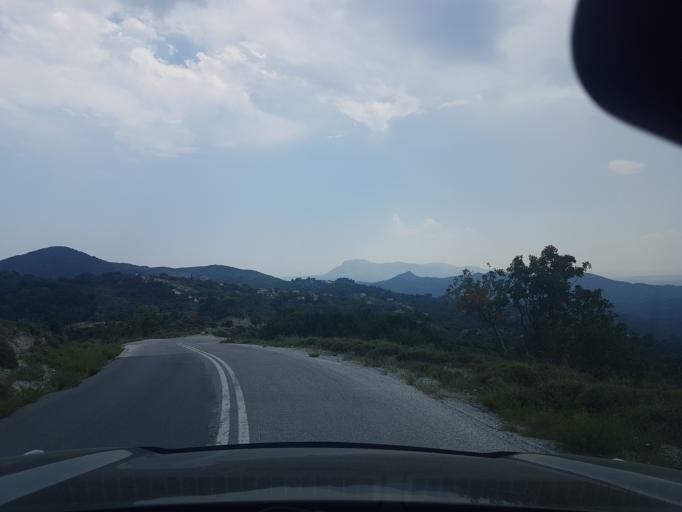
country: GR
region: Central Greece
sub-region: Nomos Evvoias
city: Kymi
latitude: 38.6431
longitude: 24.0623
